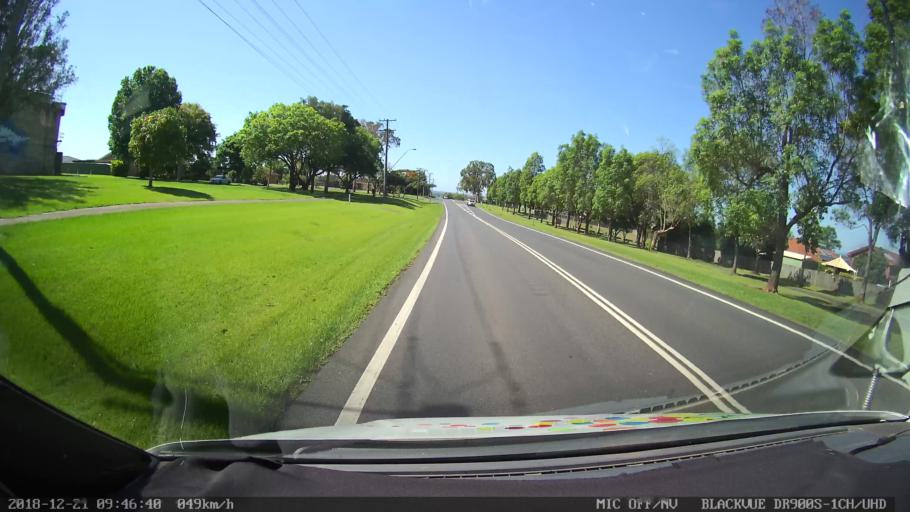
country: AU
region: New South Wales
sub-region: Clarence Valley
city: Grafton
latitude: -29.6400
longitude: 152.9259
